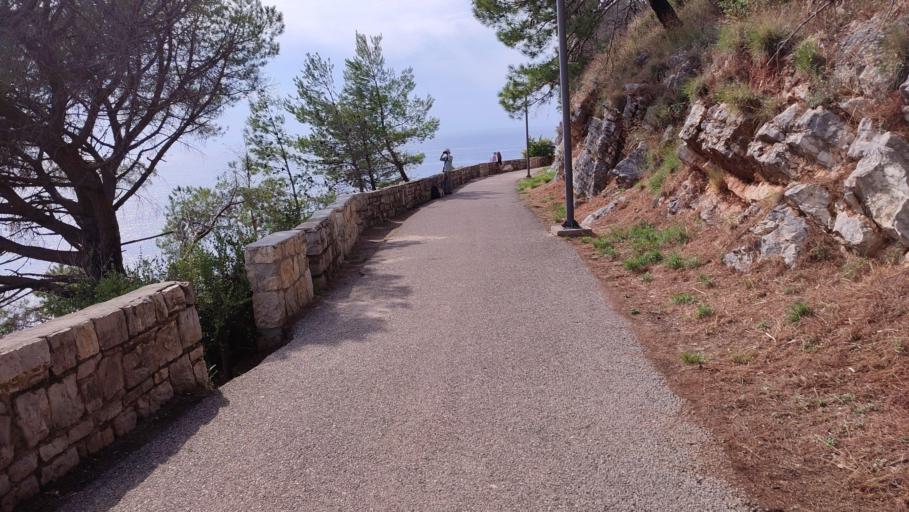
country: ME
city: Petrovac na Moru
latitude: 42.2068
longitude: 18.9308
